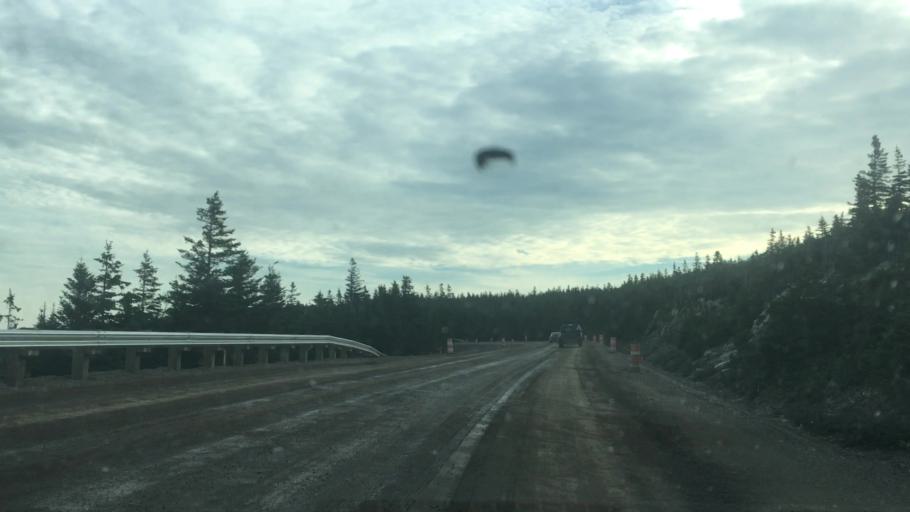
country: CA
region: Nova Scotia
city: Sydney Mines
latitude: 46.8082
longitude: -60.8427
